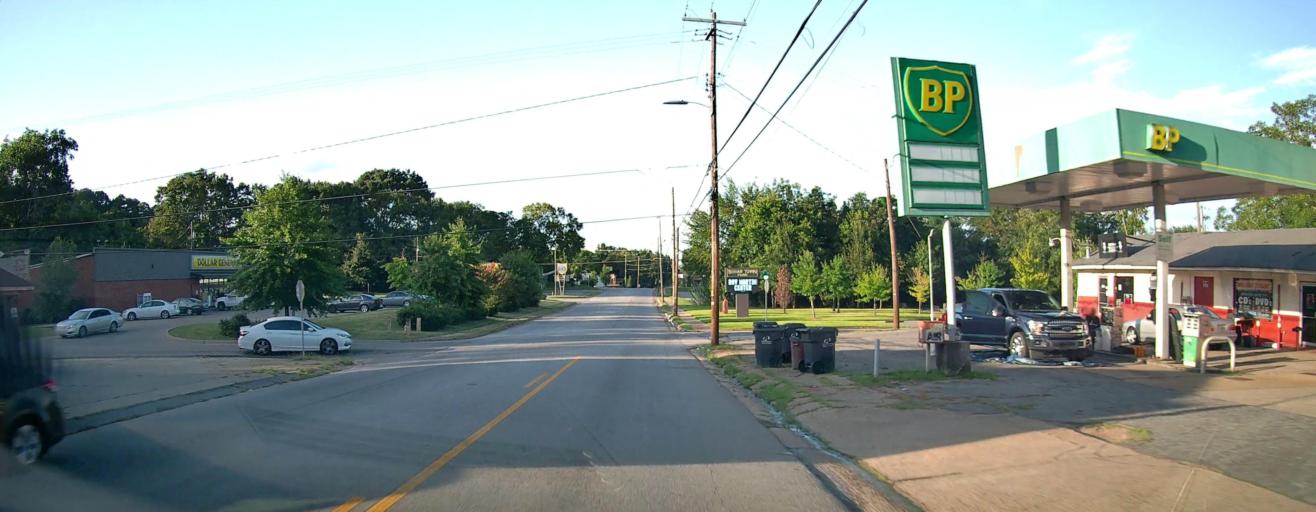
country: US
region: Alabama
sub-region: Russell County
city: Phenix City
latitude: 32.4468
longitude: -85.0091
